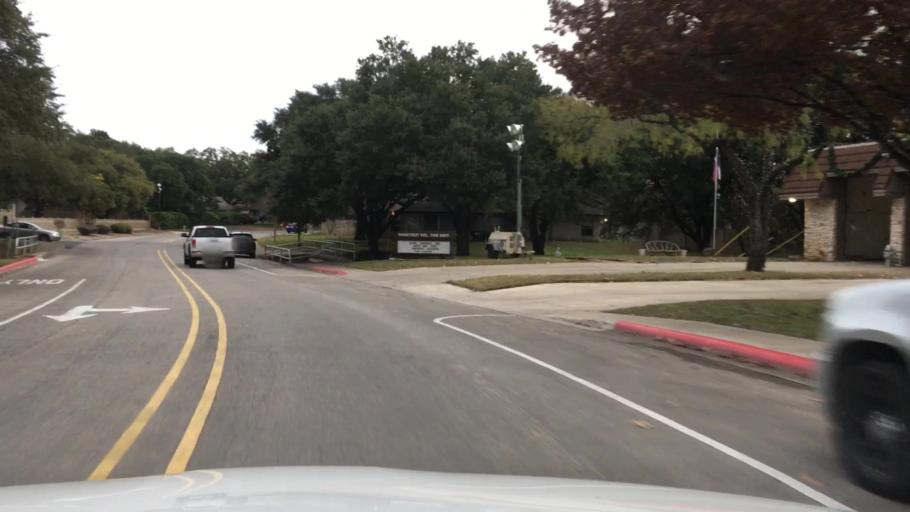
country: US
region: Texas
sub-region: Bexar County
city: Windcrest
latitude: 29.5169
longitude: -98.3814
